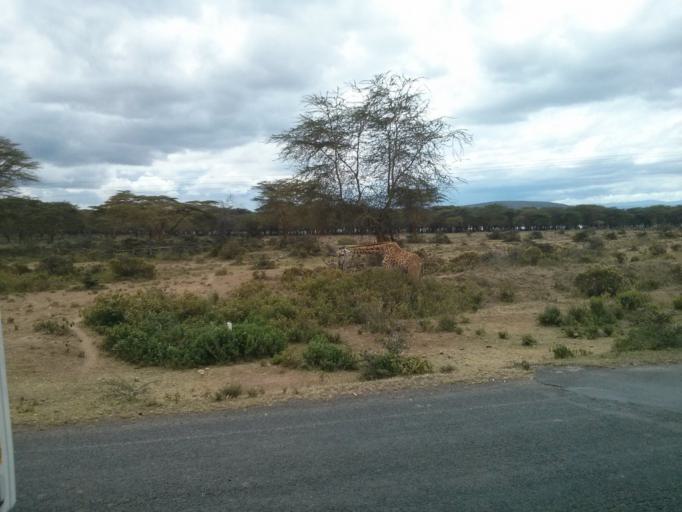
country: KE
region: Nakuru
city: Naivasha
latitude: -0.7147
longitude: 36.4315
